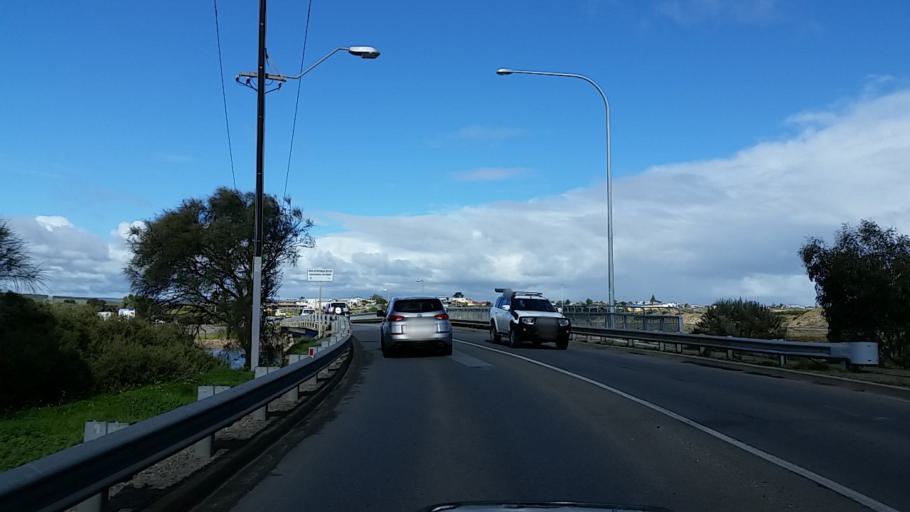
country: AU
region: South Australia
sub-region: Adelaide
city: Port Noarlunga
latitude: -35.1513
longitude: 138.4724
